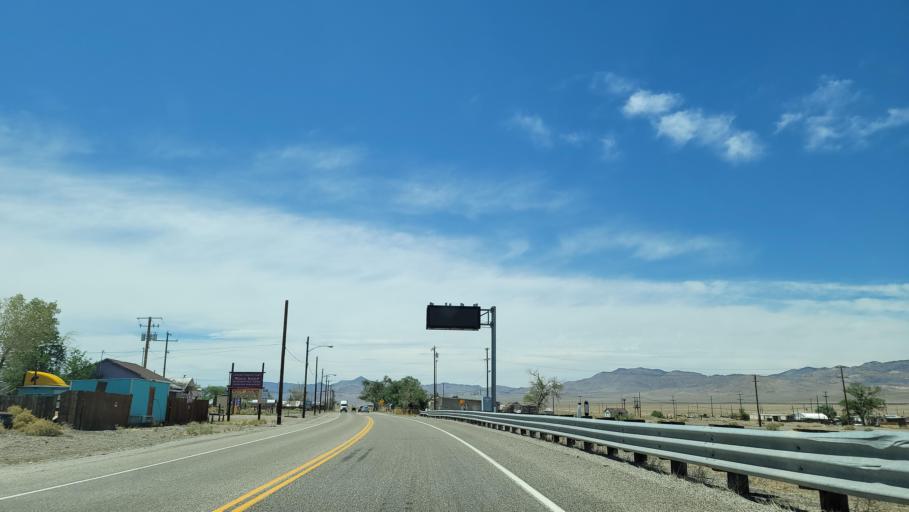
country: US
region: Nevada
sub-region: Mineral County
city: Hawthorne
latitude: 38.5040
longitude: -118.1765
